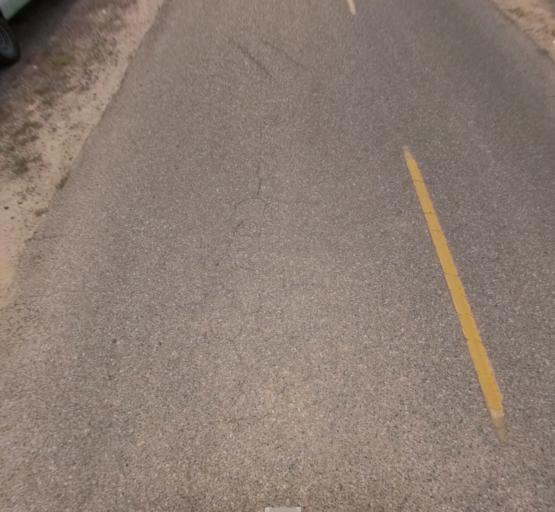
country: US
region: California
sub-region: Madera County
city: Madera Acres
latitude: 37.0163
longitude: -120.0614
